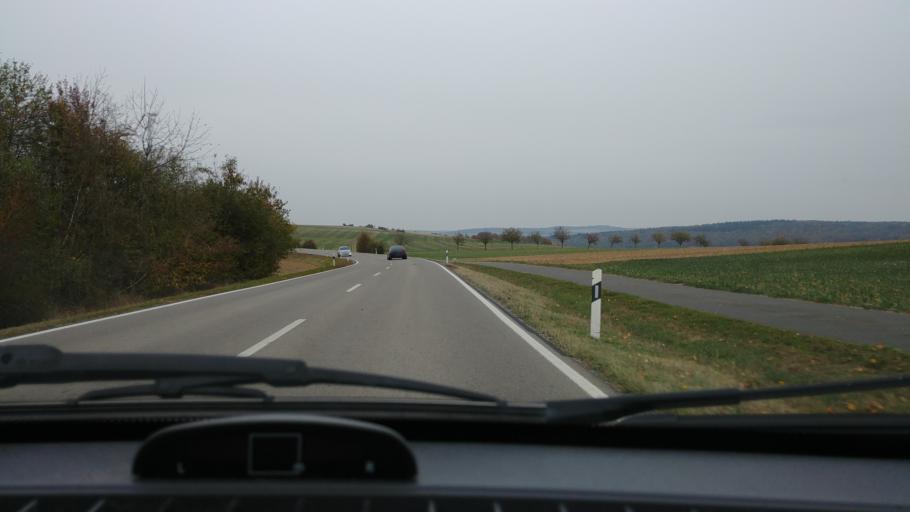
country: DE
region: Baden-Wuerttemberg
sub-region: Regierungsbezirk Stuttgart
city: Igersheim
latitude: 49.4334
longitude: 9.8087
